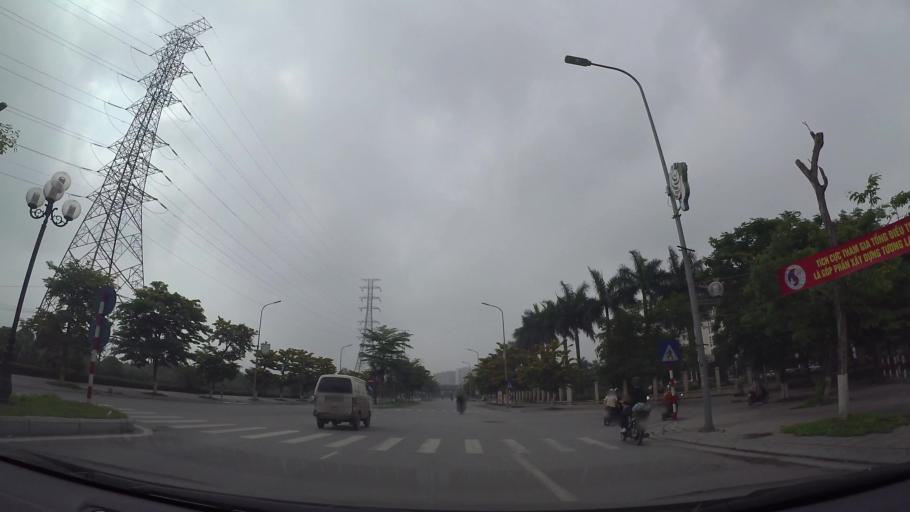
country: VN
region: Ha Noi
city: Van Dien
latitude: 20.9690
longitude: 105.8491
